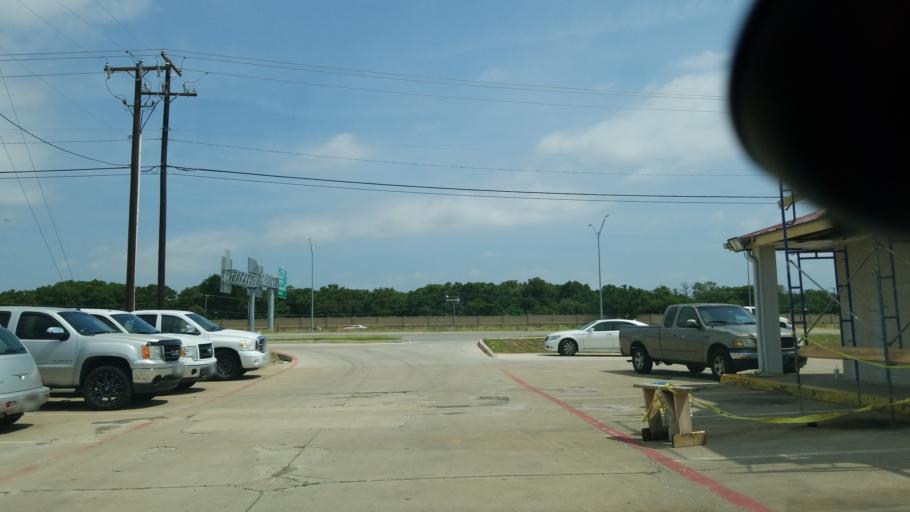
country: US
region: Texas
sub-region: Dallas County
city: Irving
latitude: 32.8362
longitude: -96.9458
